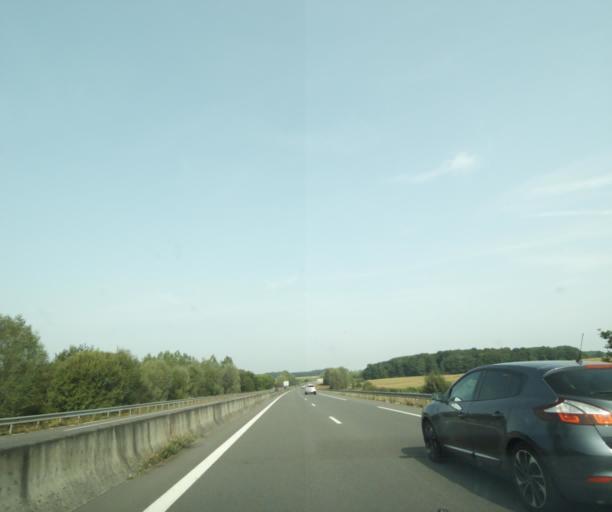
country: FR
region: Pays de la Loire
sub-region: Departement de la Sarthe
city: Champfleur
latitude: 48.3295
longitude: 0.1128
